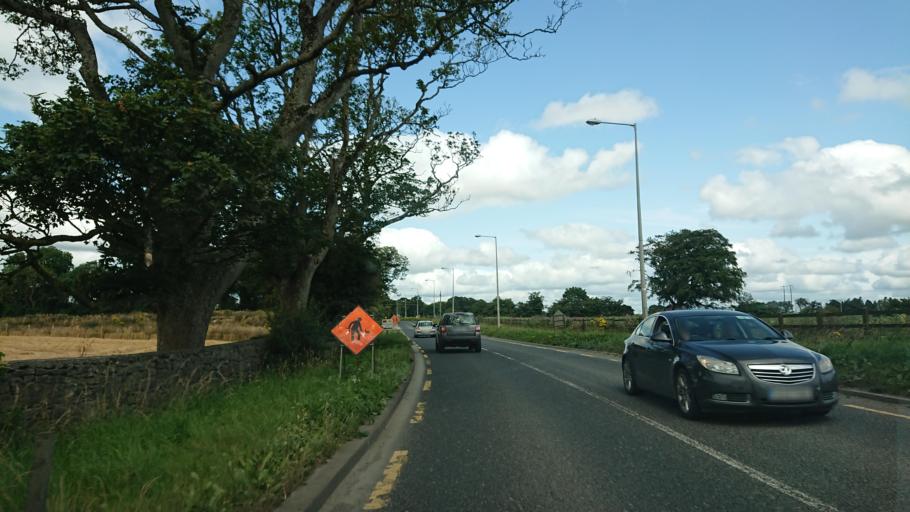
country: IE
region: Leinster
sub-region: Kildare
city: Sallins
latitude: 53.2608
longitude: -6.6685
